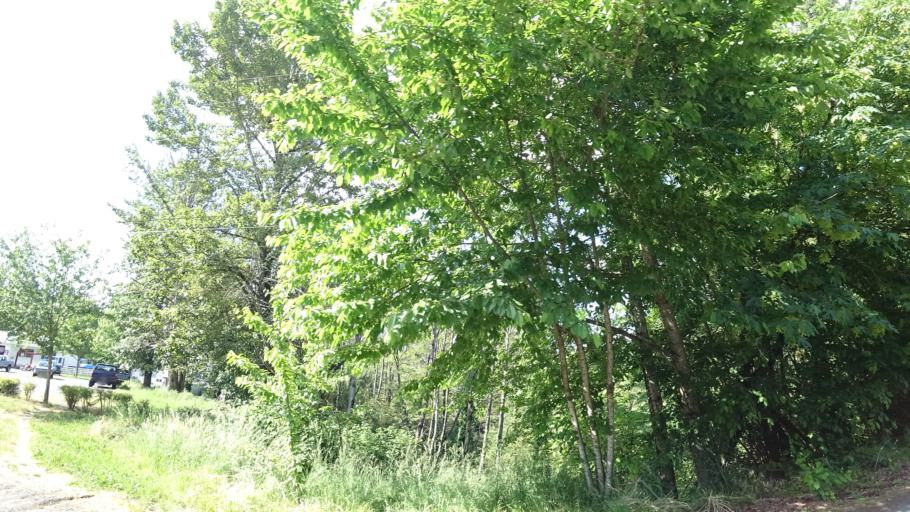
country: US
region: Oregon
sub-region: Washington County
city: Garden Home-Whitford
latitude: 45.4674
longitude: -122.7218
